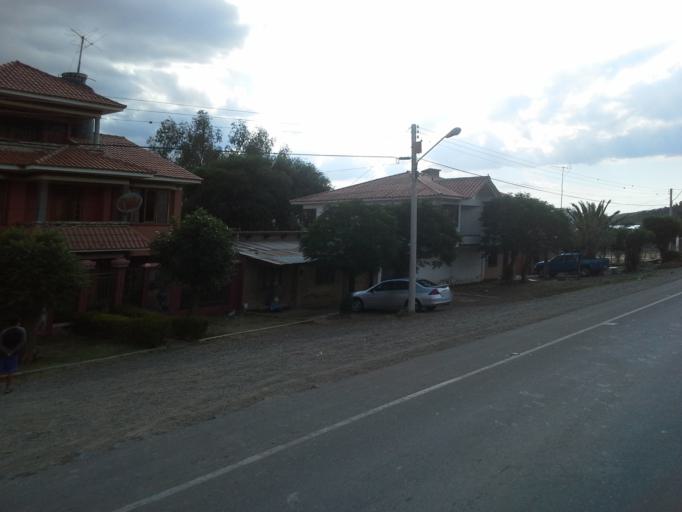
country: BO
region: Cochabamba
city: Tarata
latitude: -17.5428
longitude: -66.0311
